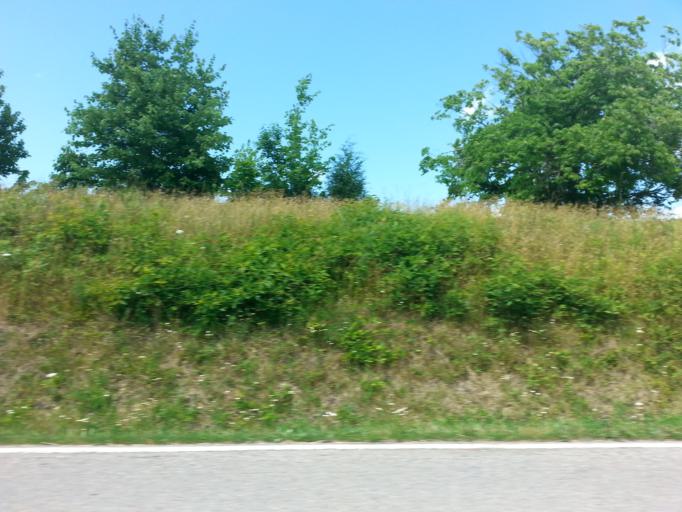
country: US
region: Virginia
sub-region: Lee County
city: Pennington Gap
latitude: 36.6974
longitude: -83.0407
